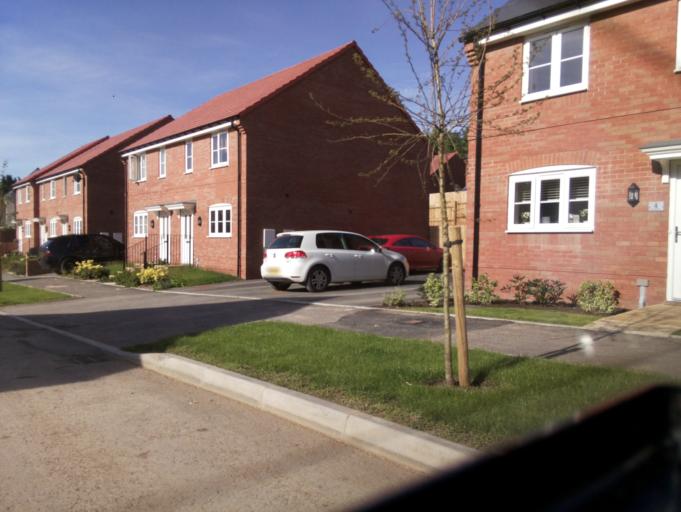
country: GB
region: England
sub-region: Bath and North East Somerset
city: Compton Dando
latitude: 51.4004
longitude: -2.5157
